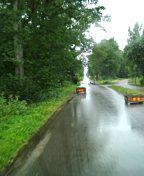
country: SE
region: Vaestmanland
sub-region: Kopings Kommun
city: Koping
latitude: 59.4851
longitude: 16.0531
